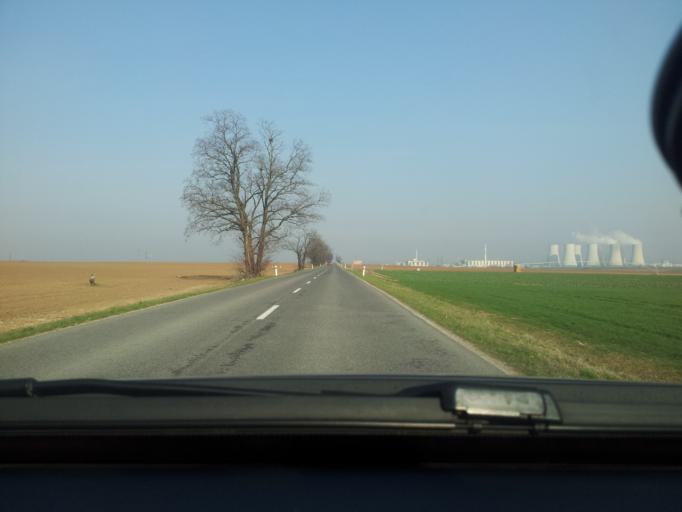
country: SK
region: Trnavsky
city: Leopoldov
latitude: 48.4668
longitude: 17.6983
